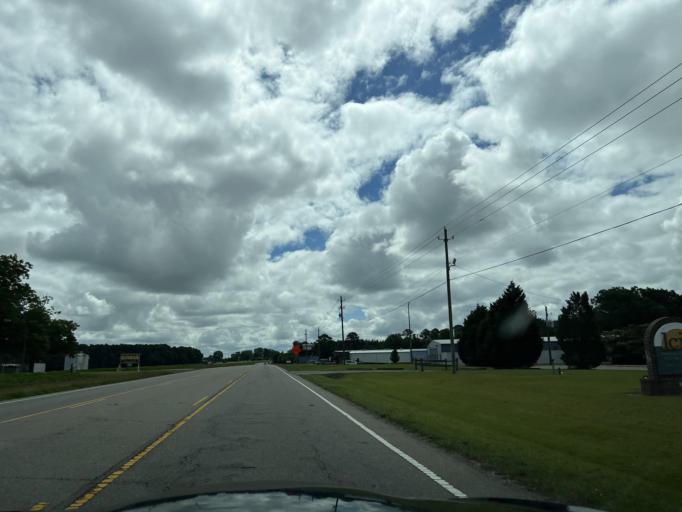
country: US
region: North Carolina
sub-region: Lee County
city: Sanford
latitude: 35.4378
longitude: -79.2020
